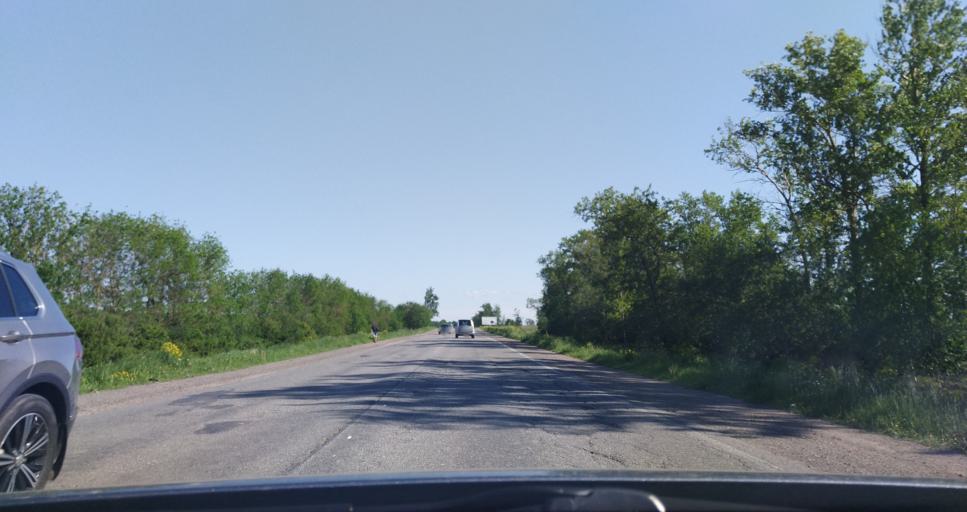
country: RU
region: St.-Petersburg
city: Krasnoye Selo
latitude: 59.7084
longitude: 30.0887
